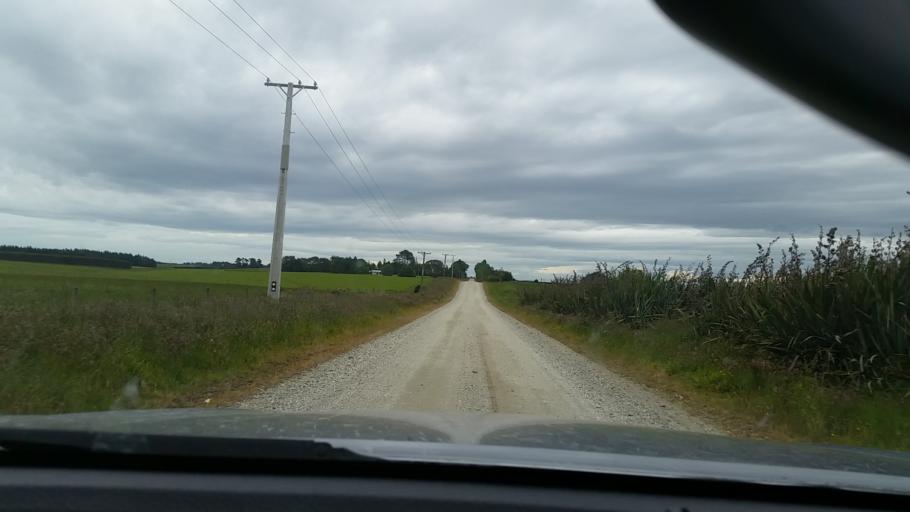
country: NZ
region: Southland
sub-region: Gore District
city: Gore
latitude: -46.2795
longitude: 168.7354
